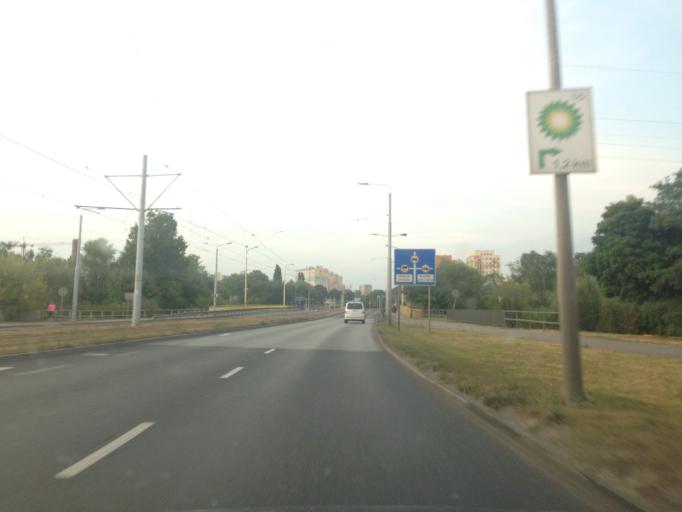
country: PL
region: Kujawsko-Pomorskie
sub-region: Bydgoszcz
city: Bydgoszcz
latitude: 53.1183
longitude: 18.0343
